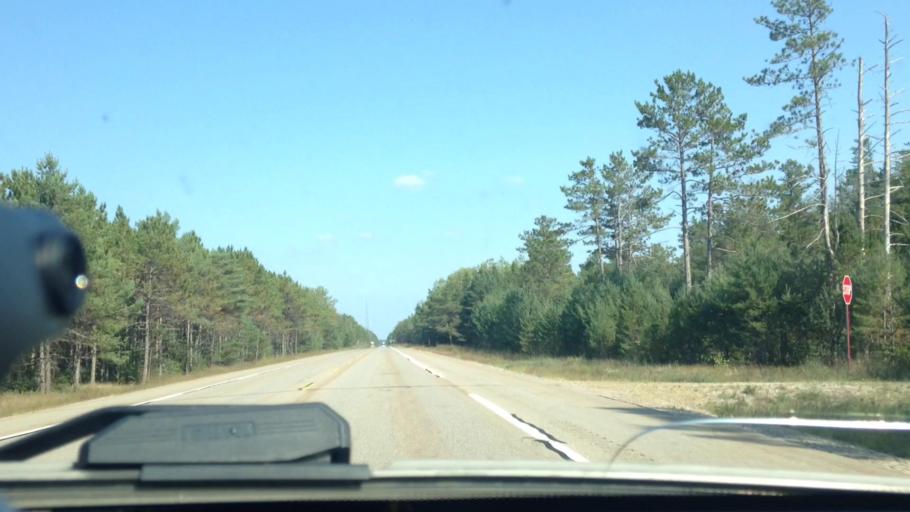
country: US
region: Michigan
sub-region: Chippewa County
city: Sault Ste. Marie
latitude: 46.3672
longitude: -84.7502
